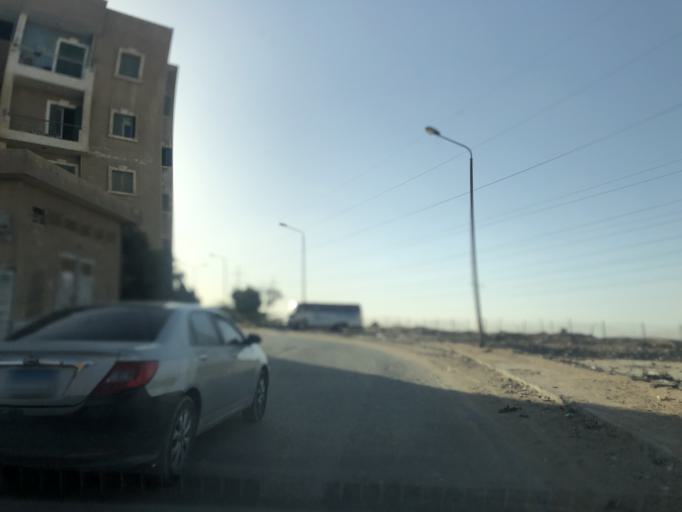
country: EG
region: Al Jizah
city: Al Jizah
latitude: 29.9885
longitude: 31.1079
